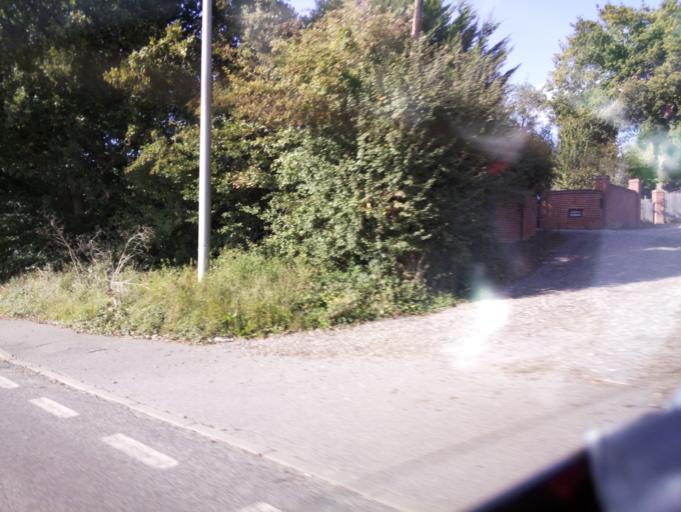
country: GB
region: England
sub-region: Hampshire
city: Tadley
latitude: 51.3959
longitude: -1.1649
